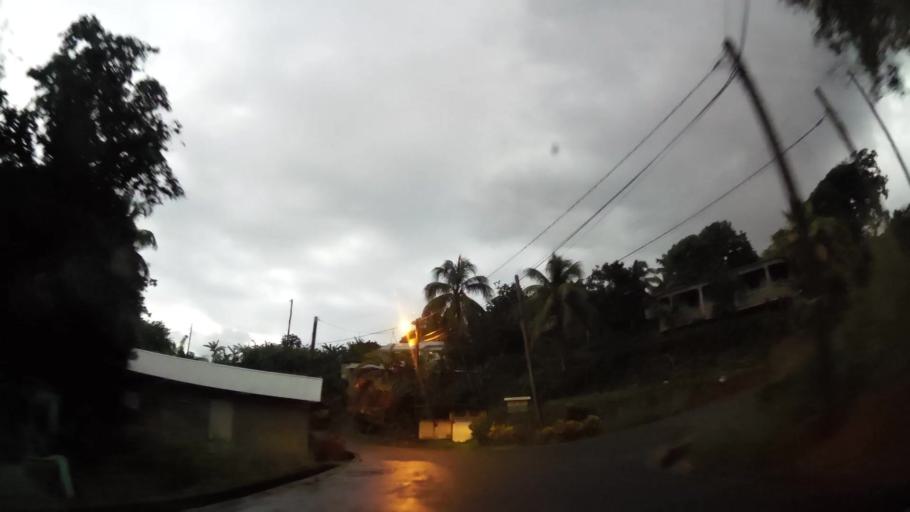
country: DM
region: Saint Andrew
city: Woodford Hill
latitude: 15.5870
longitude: -61.3295
